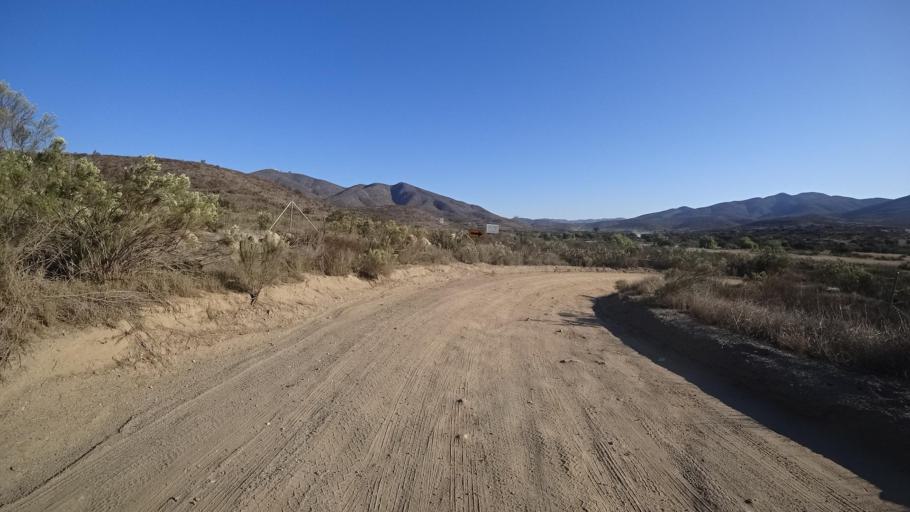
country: US
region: California
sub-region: San Diego County
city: Jamul
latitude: 32.6644
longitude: -116.9309
